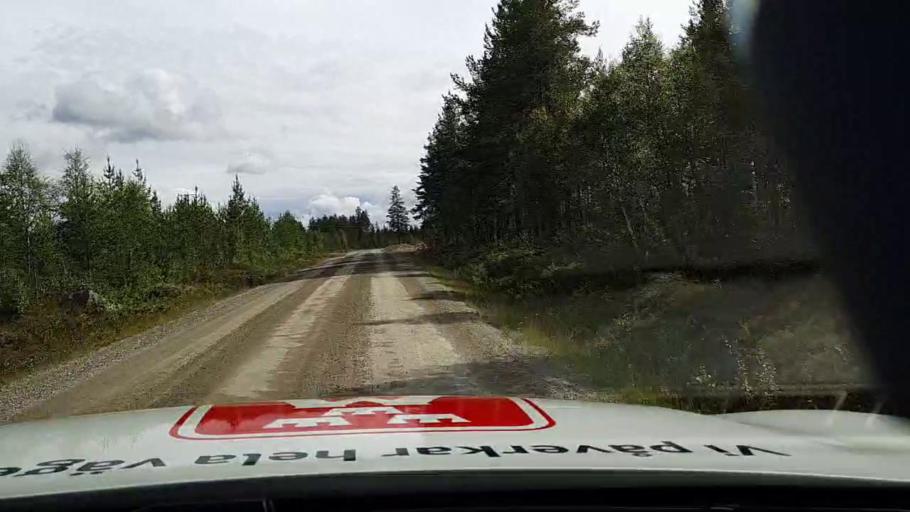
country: SE
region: Jaemtland
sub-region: Are Kommun
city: Jarpen
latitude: 62.5041
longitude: 13.5000
